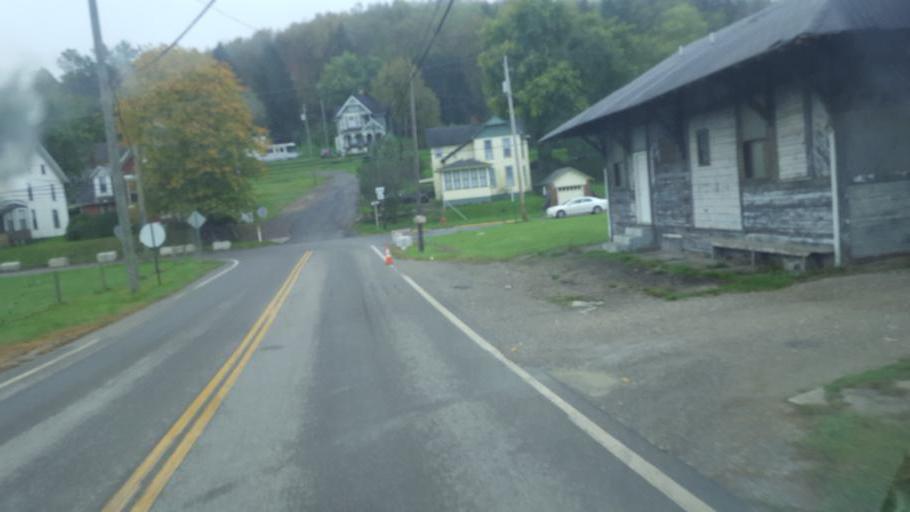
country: US
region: Ohio
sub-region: Harrison County
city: Cadiz
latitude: 40.3930
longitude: -81.0849
